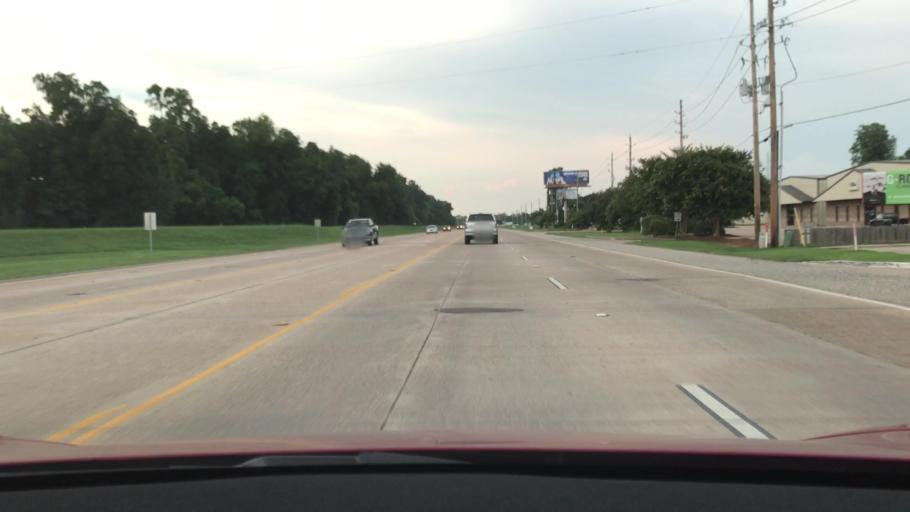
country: US
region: Louisiana
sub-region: Bossier Parish
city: Bossier City
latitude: 32.4505
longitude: -93.6964
